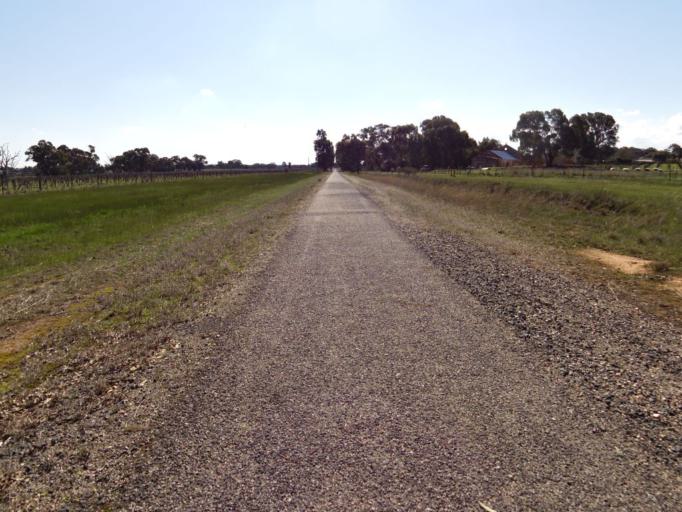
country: AU
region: New South Wales
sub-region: Corowa Shire
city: Corowa
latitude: -36.0482
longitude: 146.4589
